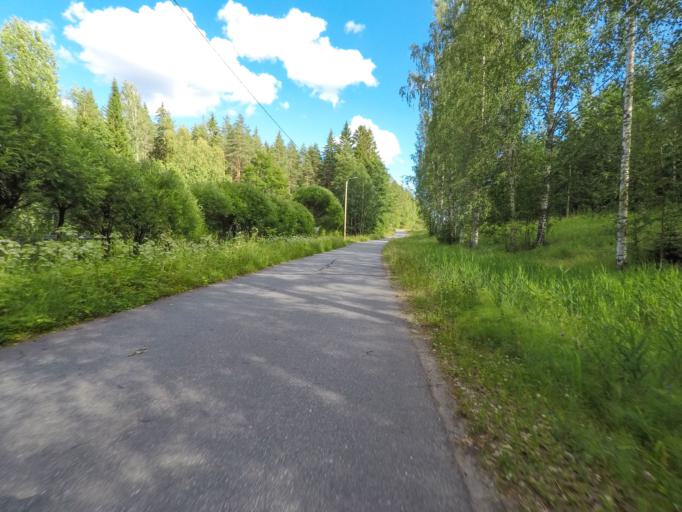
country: FI
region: South Karelia
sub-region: Lappeenranta
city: Lappeenranta
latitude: 61.1050
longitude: 28.1213
